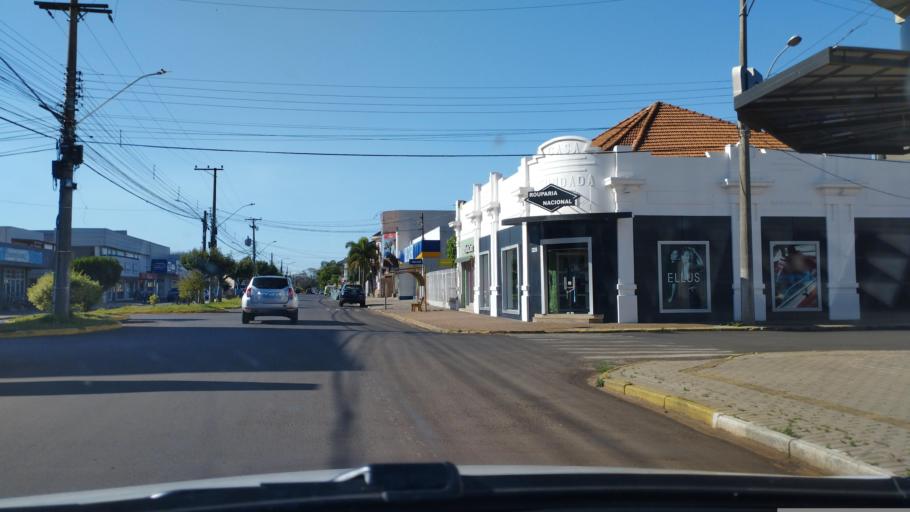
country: BR
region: Rio Grande do Sul
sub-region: Tupancireta
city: Tupancireta
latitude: -29.0803
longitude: -53.8370
